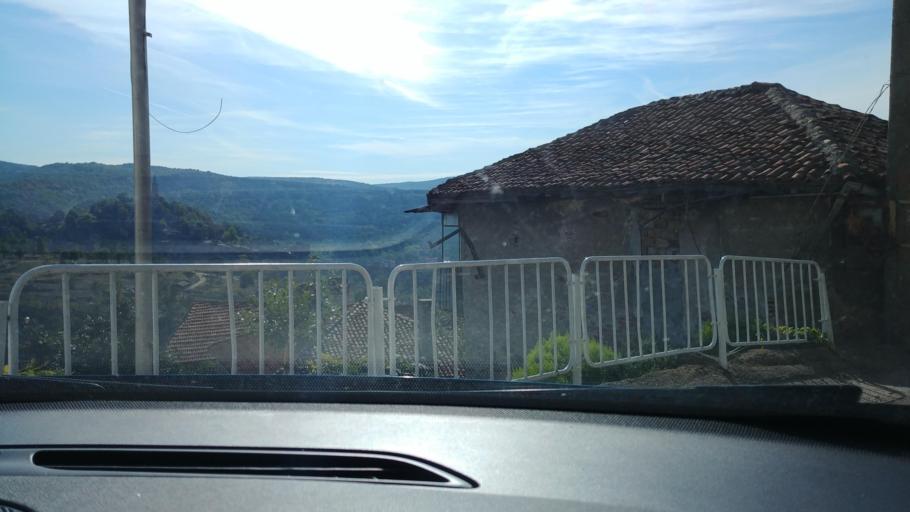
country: BG
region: Veliko Turnovo
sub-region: Obshtina Veliko Turnovo
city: Veliko Turnovo
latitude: 43.0862
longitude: 25.6405
